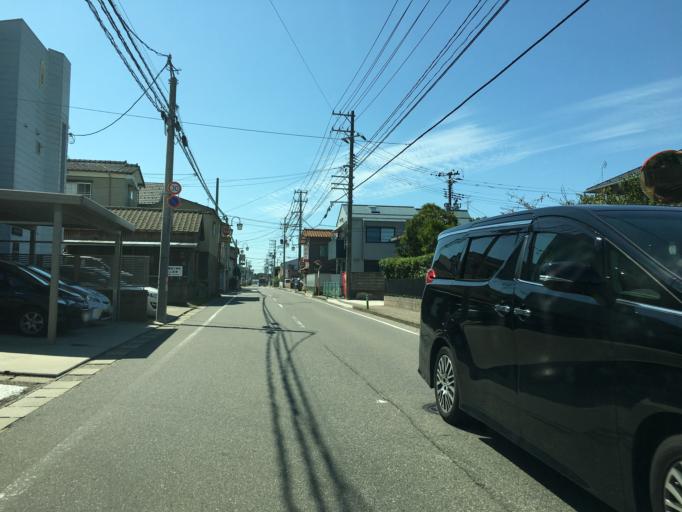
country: JP
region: Niigata
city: Niigata-shi
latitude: 37.9003
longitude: 138.9974
